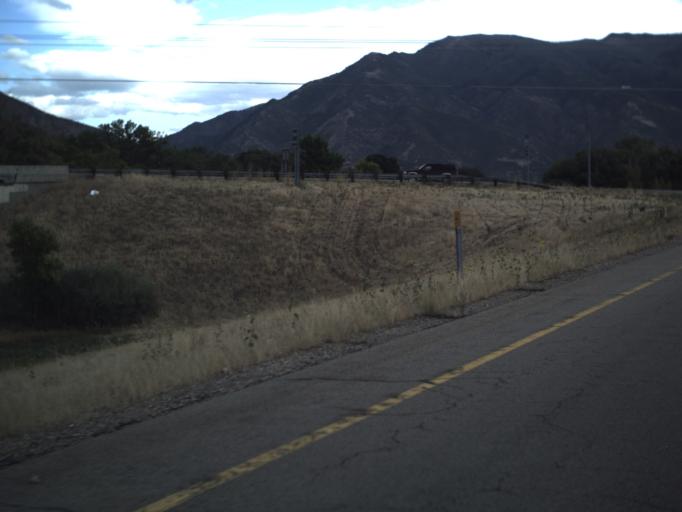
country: US
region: Utah
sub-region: Weber County
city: Washington Terrace
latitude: 41.1496
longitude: -111.9702
